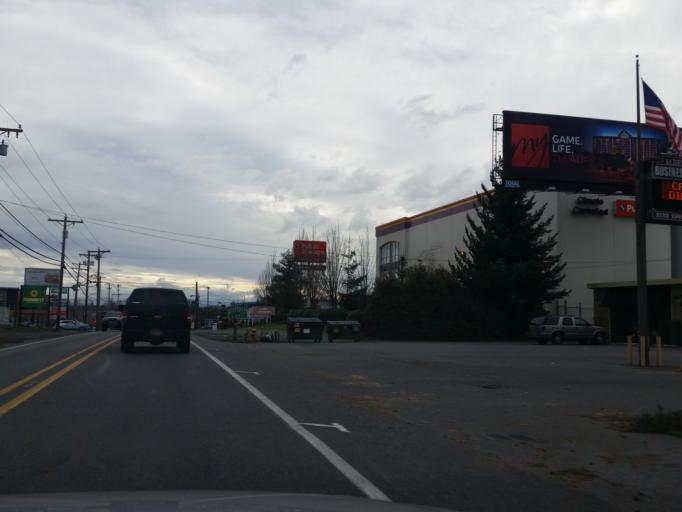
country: US
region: Washington
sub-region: Snohomish County
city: Alderwood Manor
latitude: 47.8207
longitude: -122.2627
